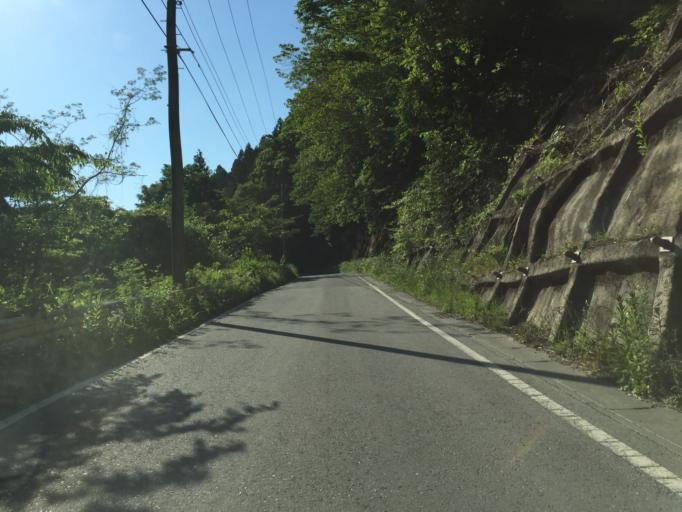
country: JP
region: Ibaraki
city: Kitaibaraki
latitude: 36.8625
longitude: 140.7191
